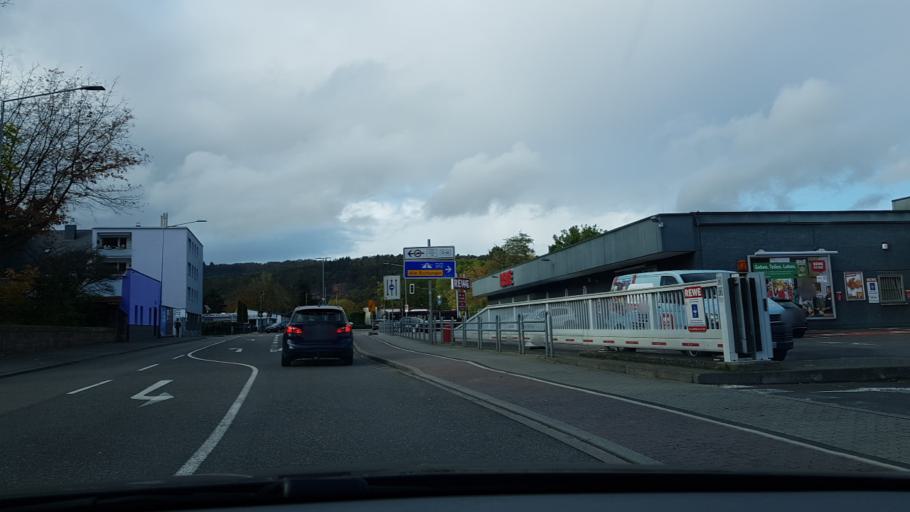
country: DE
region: Rheinland-Pfalz
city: Trier
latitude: 49.7646
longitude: 6.6552
